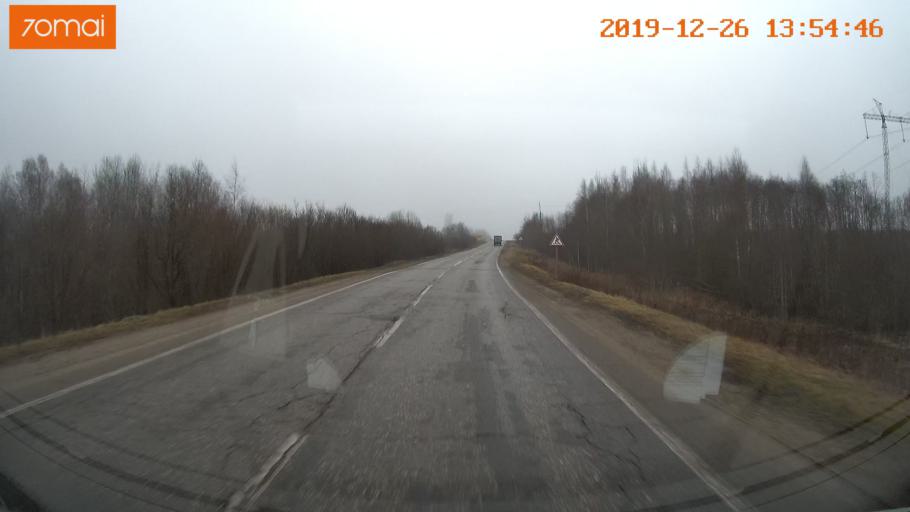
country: RU
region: Jaroslavl
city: Poshekhon'ye
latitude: 58.6103
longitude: 38.6391
